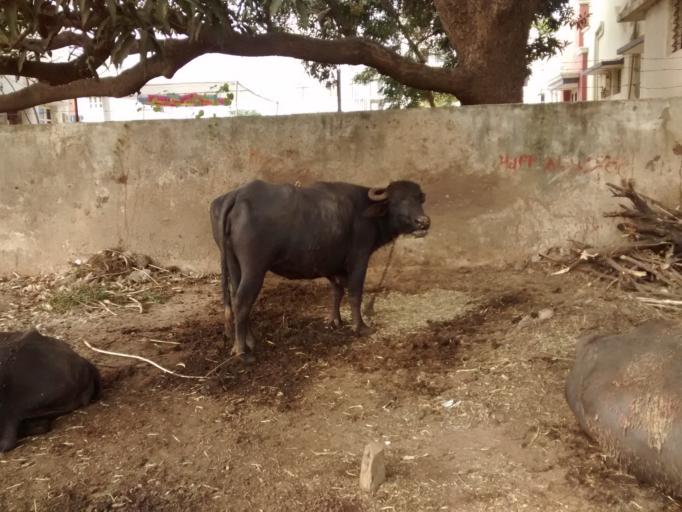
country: IN
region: Gujarat
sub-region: Gandhinagar
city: Dahegam
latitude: 23.1607
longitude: 72.8082
